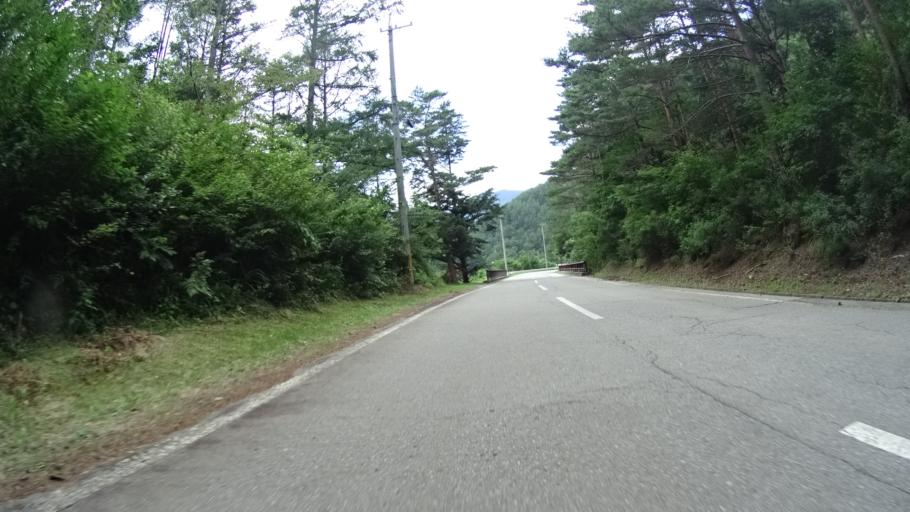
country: JP
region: Nagano
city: Saku
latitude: 36.0702
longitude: 138.6164
